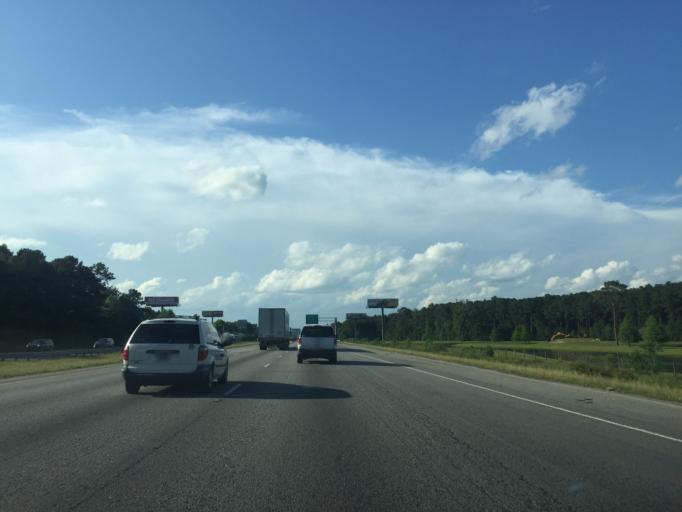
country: US
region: Georgia
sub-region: Chatham County
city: Pooler
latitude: 32.1203
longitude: -81.2385
